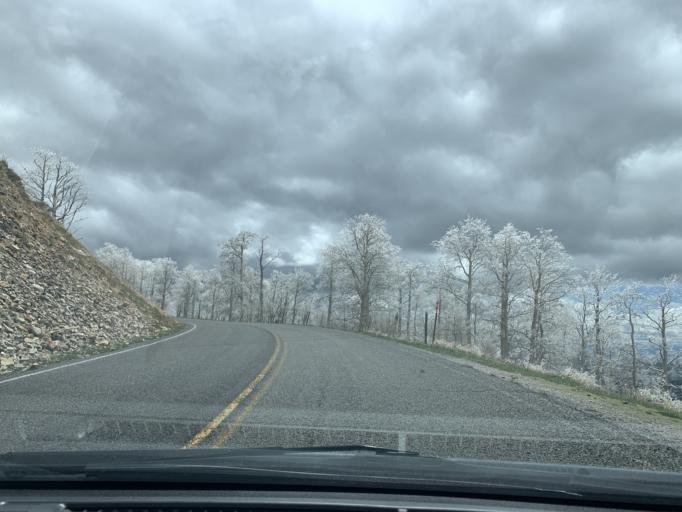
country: US
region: Utah
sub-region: Utah County
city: Santaquin
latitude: 39.8497
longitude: -111.7052
